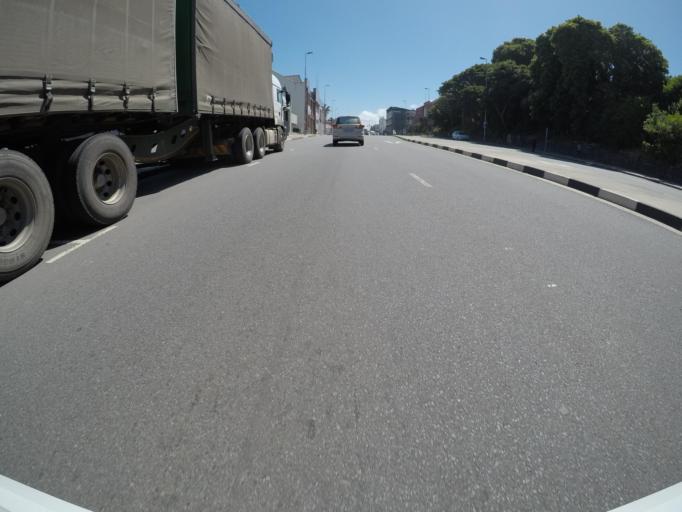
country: ZA
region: Eastern Cape
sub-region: Buffalo City Metropolitan Municipality
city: East London
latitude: -33.0186
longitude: 27.9096
